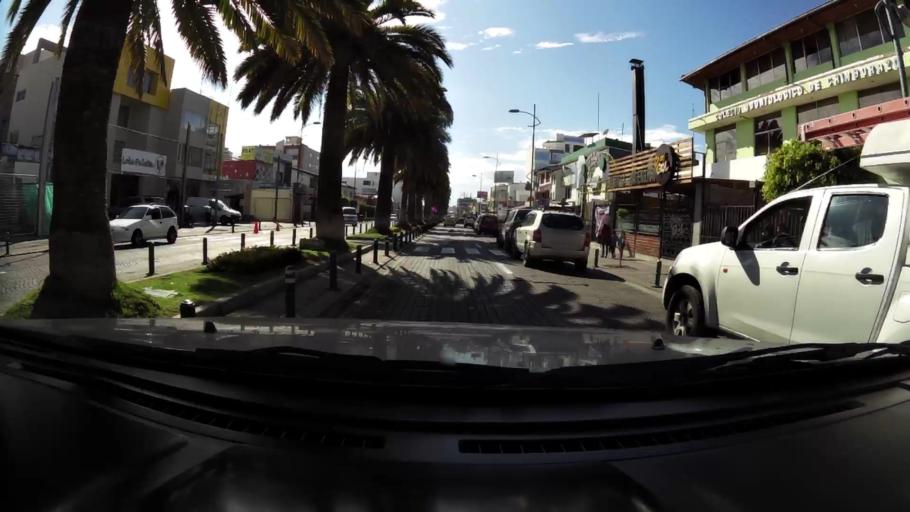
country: EC
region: Chimborazo
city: Riobamba
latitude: -1.6660
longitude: -78.6578
